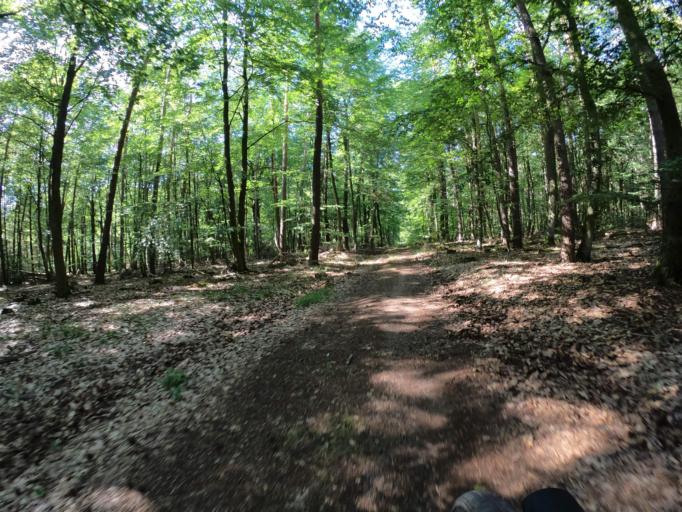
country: DE
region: Hesse
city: Langen
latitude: 49.9916
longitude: 8.6272
